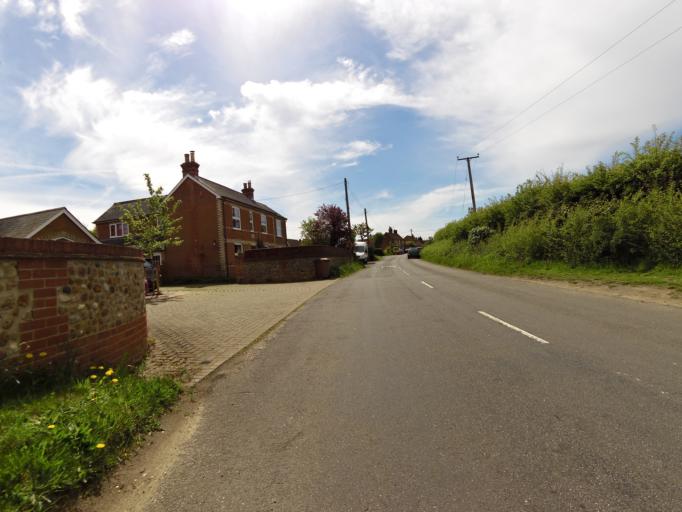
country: GB
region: England
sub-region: Essex
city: Mistley
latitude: 52.0025
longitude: 1.1134
